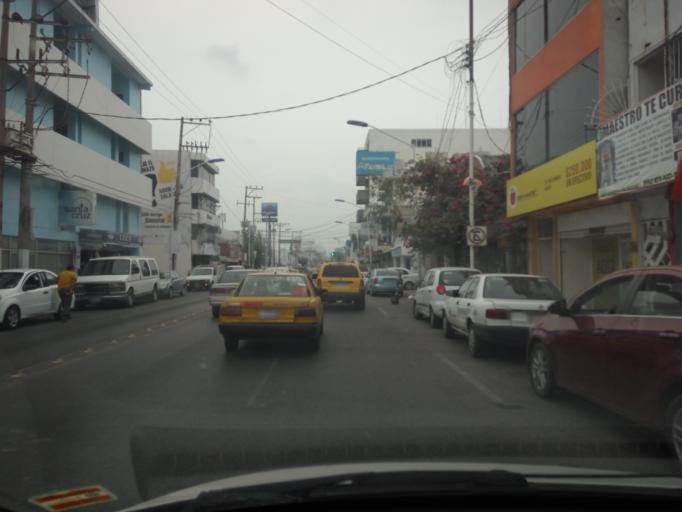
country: MX
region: Tabasco
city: Villahermosa
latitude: 17.9931
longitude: -92.9188
